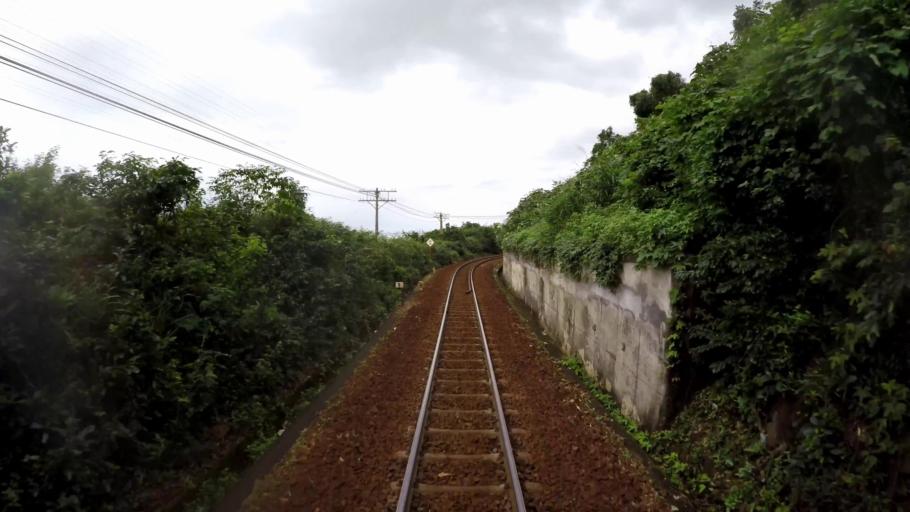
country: VN
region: Da Nang
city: Lien Chieu
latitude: 16.1588
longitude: 108.1349
